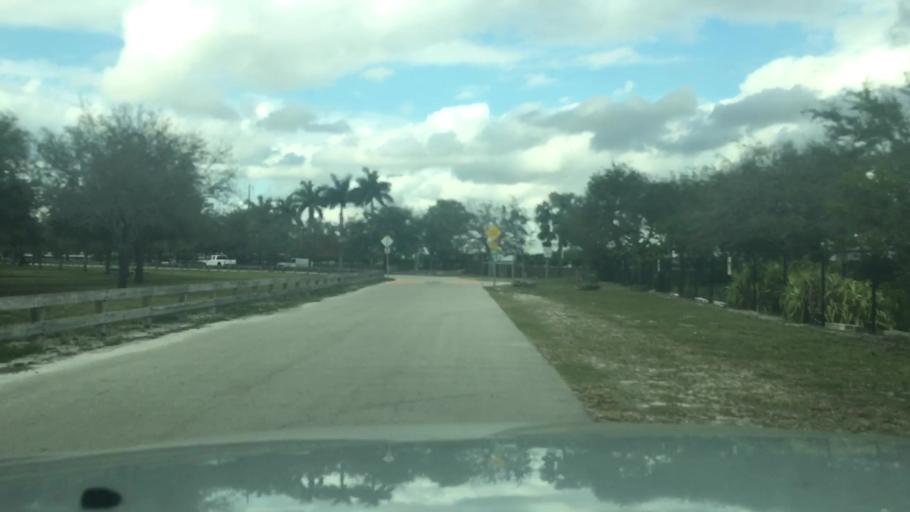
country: US
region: Florida
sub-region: Miami-Dade County
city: Opa-locka
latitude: 25.8881
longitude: -80.2751
